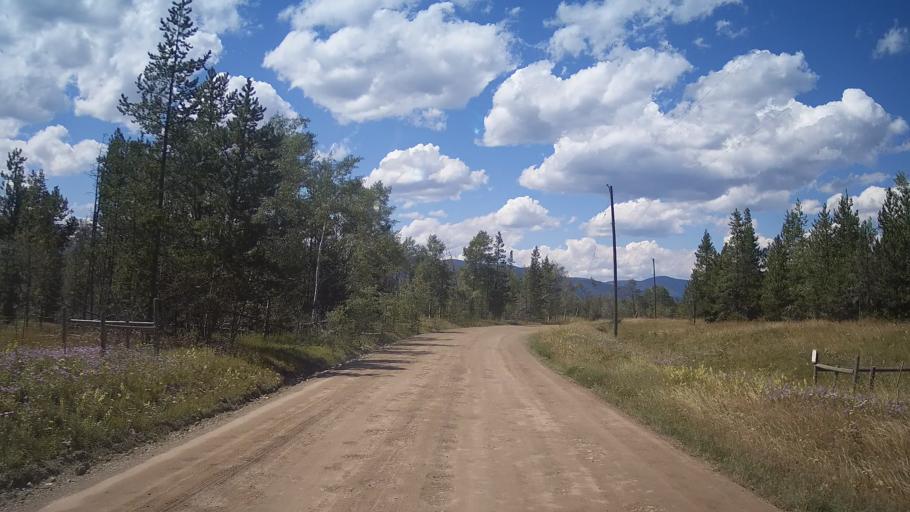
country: CA
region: British Columbia
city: Cache Creek
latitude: 51.2582
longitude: -121.6854
